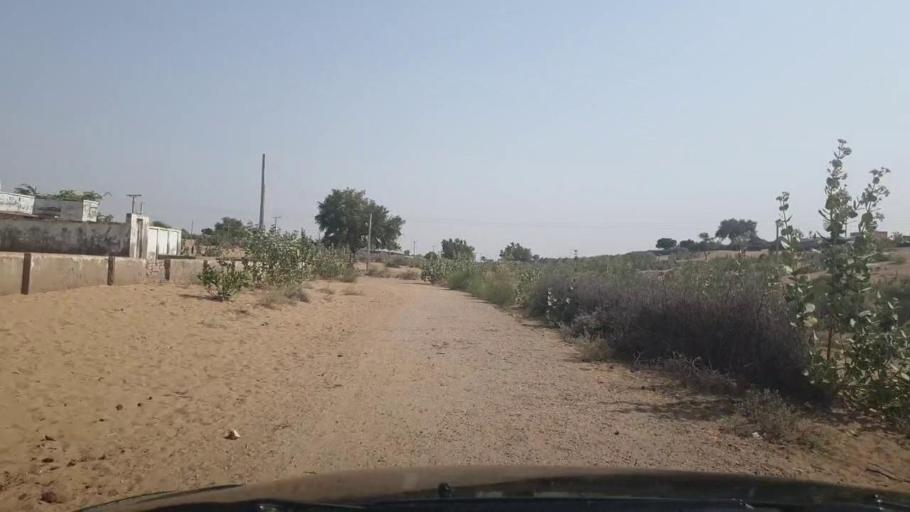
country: PK
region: Sindh
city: Islamkot
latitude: 25.0551
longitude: 70.2121
